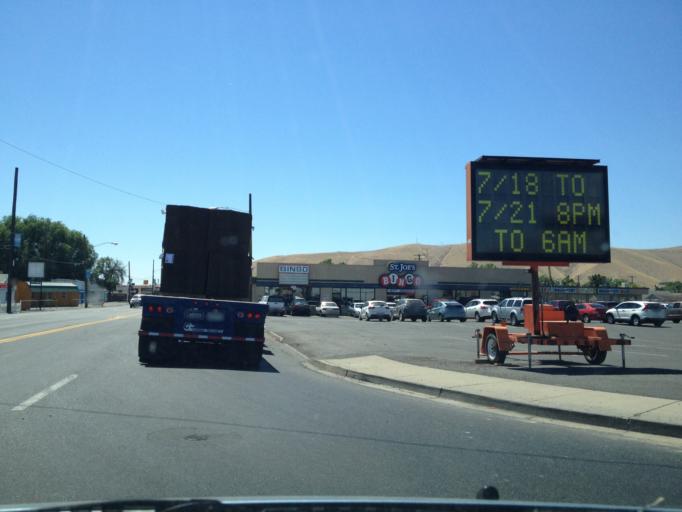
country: US
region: Washington
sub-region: Yakima County
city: Union Gap
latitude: 46.5572
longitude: -120.4754
